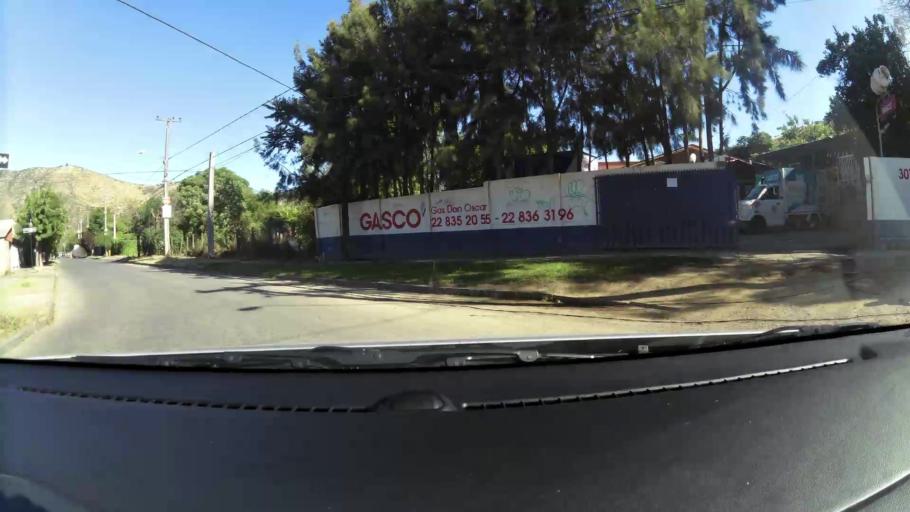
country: CL
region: Santiago Metropolitan
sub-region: Provincia de Chacabuco
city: Lampa
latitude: -33.3990
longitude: -71.1212
